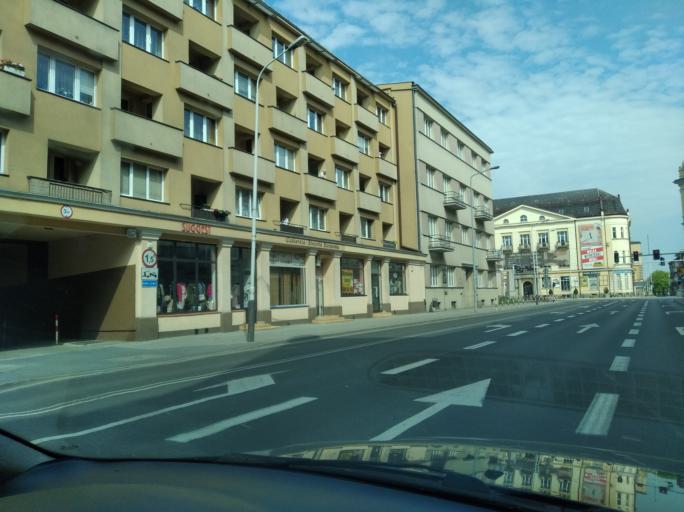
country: PL
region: Subcarpathian Voivodeship
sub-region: Powiat jaroslawski
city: Jaroslaw
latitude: 50.0153
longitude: 22.6779
